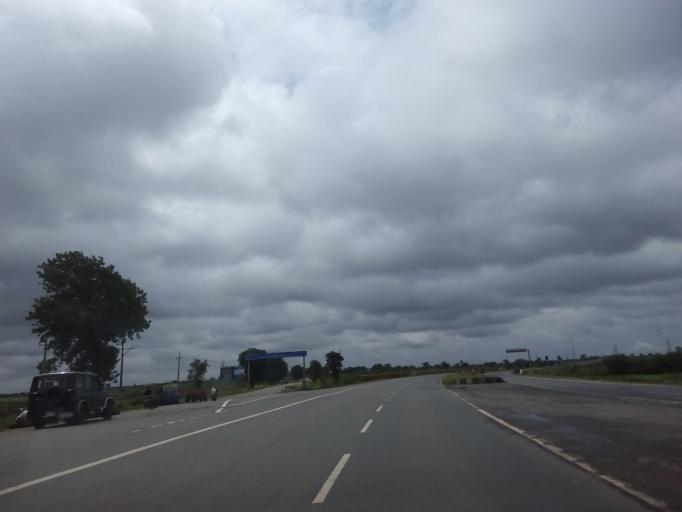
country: IN
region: Karnataka
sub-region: Haveri
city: Haveri
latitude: 14.8263
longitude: 75.3672
